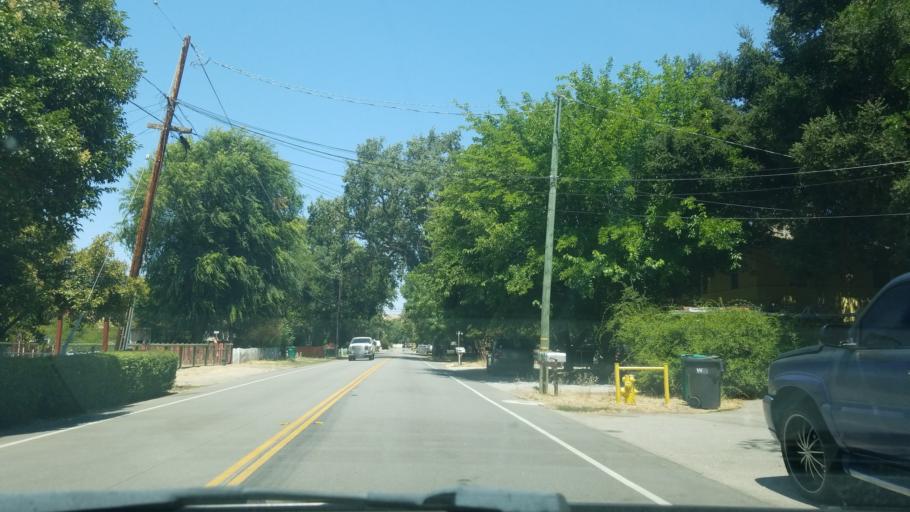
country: US
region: California
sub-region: San Luis Obispo County
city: Atascadero
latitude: 35.4963
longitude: -120.6638
